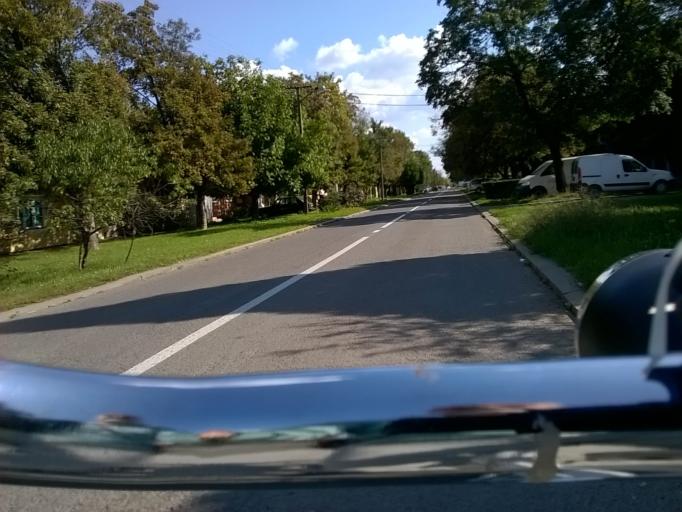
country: RS
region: Autonomna Pokrajina Vojvodina
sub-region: Juznobanatski Okrug
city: Pancevo
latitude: 44.8810
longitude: 20.6402
